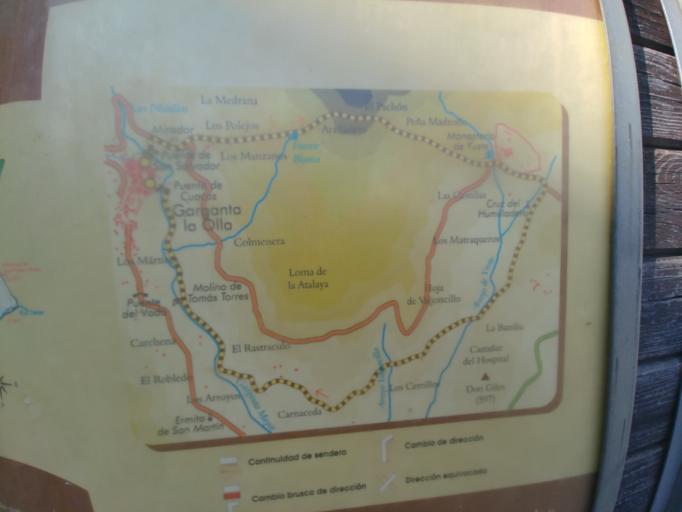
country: ES
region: Extremadura
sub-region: Provincia de Caceres
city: Garganta la Olla
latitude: 40.1109
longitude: -5.7748
